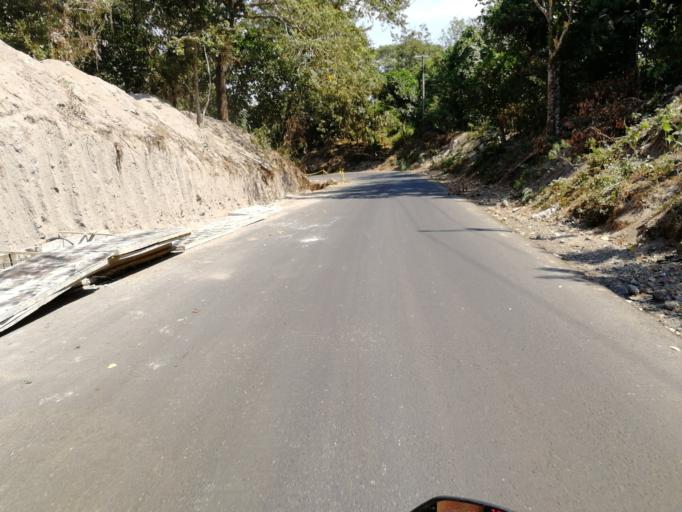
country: ID
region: West Nusa Tenggara
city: Lelongken
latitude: -8.3299
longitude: 116.4970
